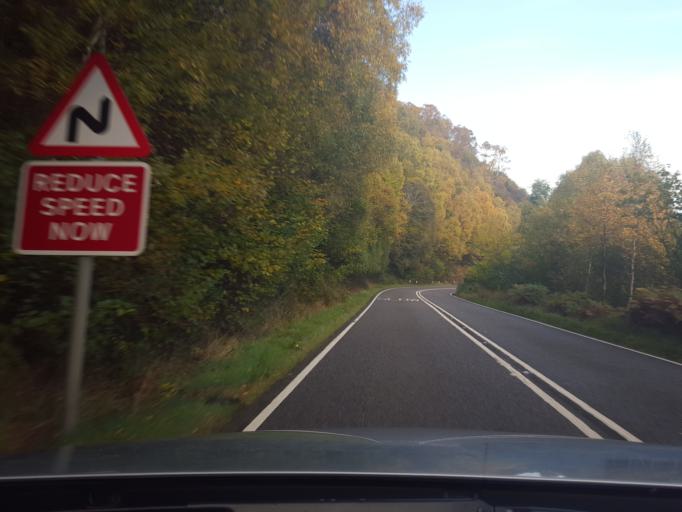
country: GB
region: Scotland
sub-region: Highland
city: Beauly
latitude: 57.3152
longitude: -4.4536
